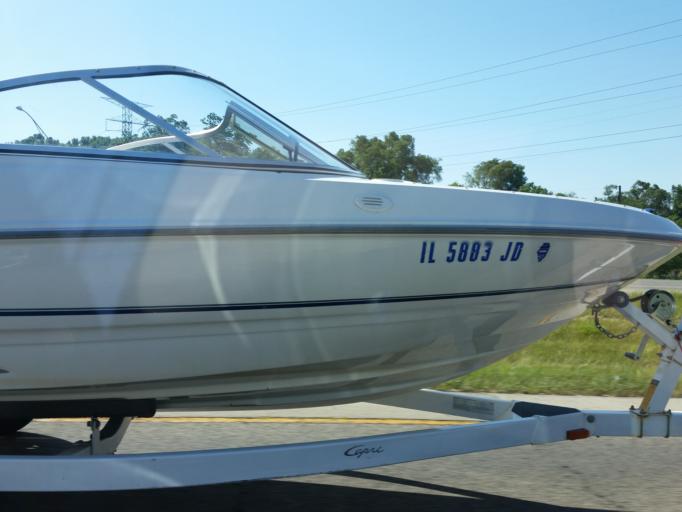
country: US
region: Illinois
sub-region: Winnebago County
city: Machesney Park
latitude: 42.3605
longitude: -89.0400
